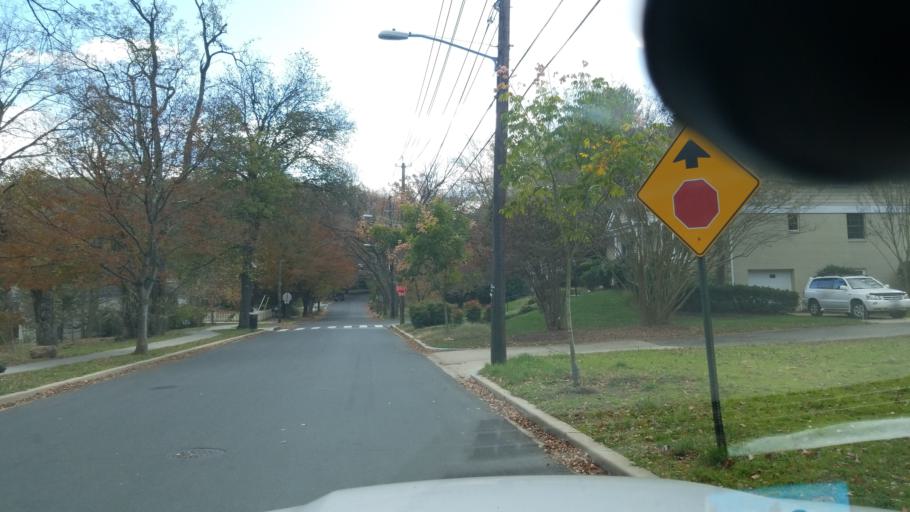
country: US
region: Maryland
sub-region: Montgomery County
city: Chevy Chase
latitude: 38.9580
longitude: -77.0649
